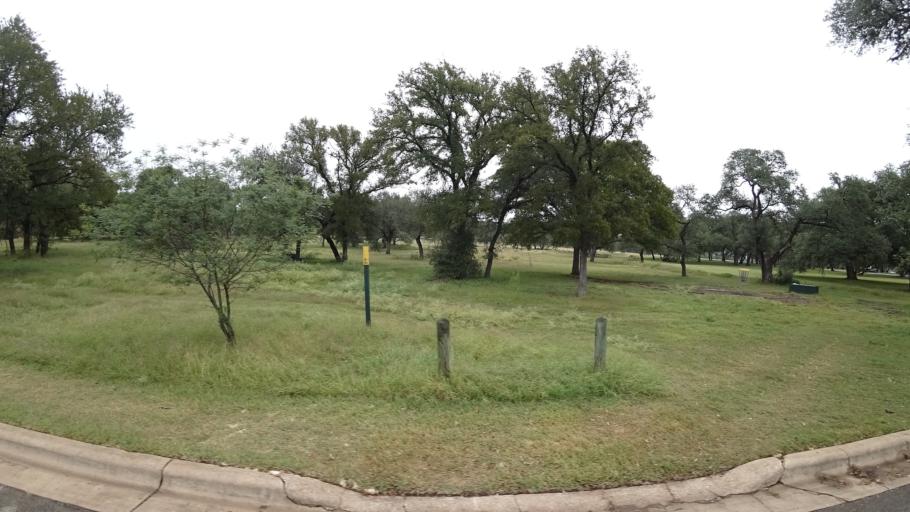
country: US
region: Texas
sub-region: Travis County
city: Rollingwood
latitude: 30.2673
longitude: -97.7756
